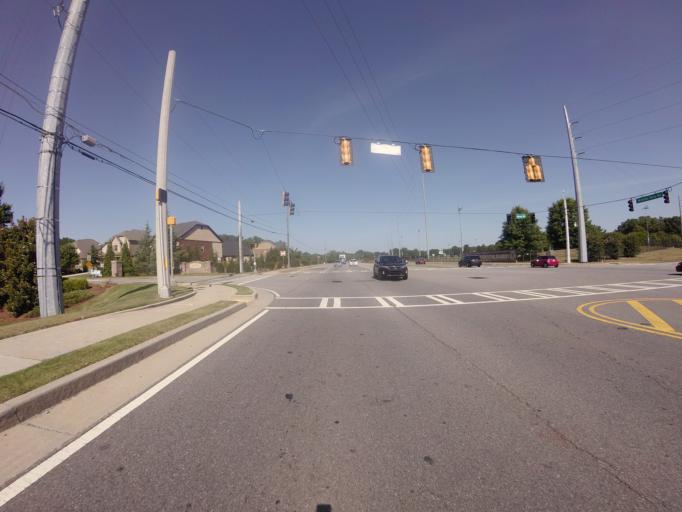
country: US
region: Georgia
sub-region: Gwinnett County
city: Suwanee
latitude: 34.0508
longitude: -84.1152
